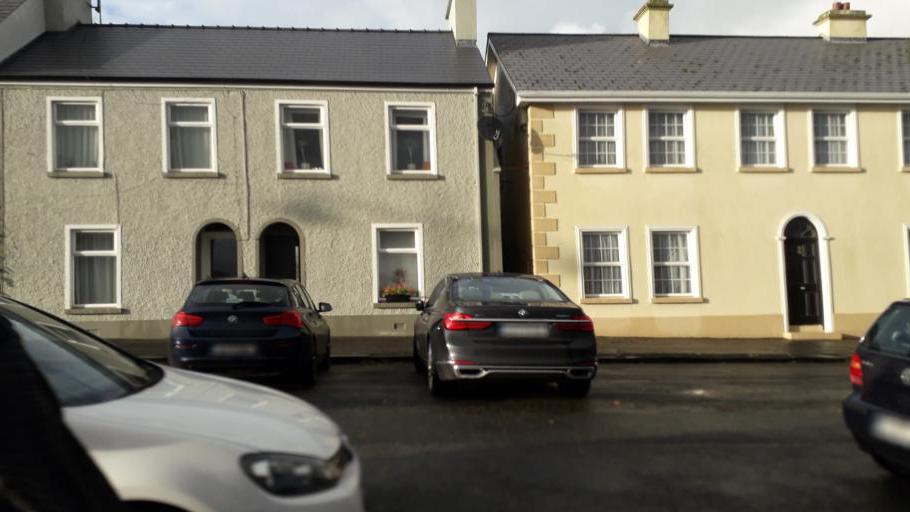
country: IE
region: Connaught
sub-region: Roscommon
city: Roscommon
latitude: 53.7768
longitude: -8.1079
